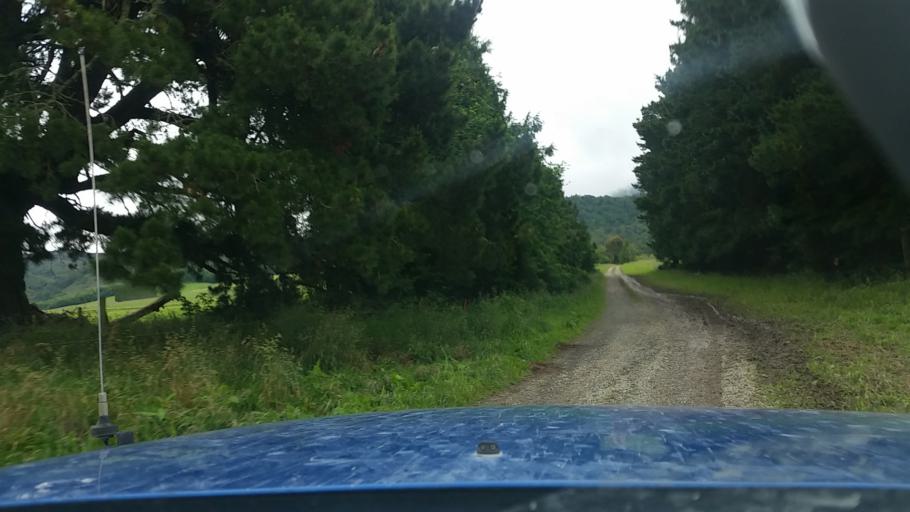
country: NZ
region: Canterbury
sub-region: Ashburton District
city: Methven
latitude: -43.6638
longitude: 171.4132
